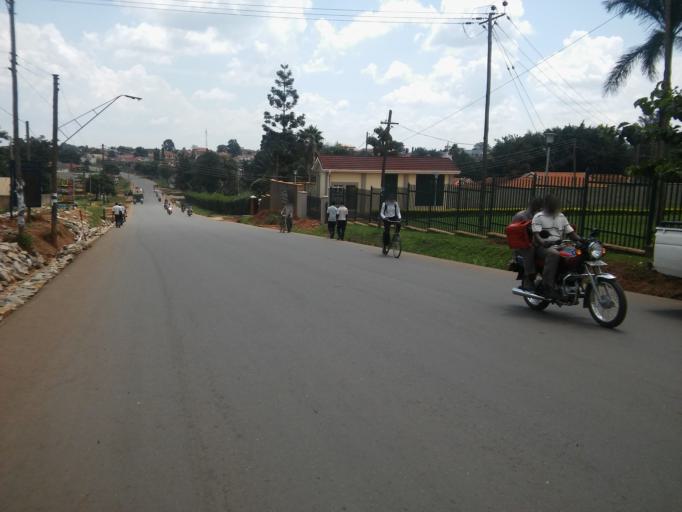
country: UG
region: Eastern Region
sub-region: Mbale District
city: Mbale
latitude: 1.0731
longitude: 34.1723
